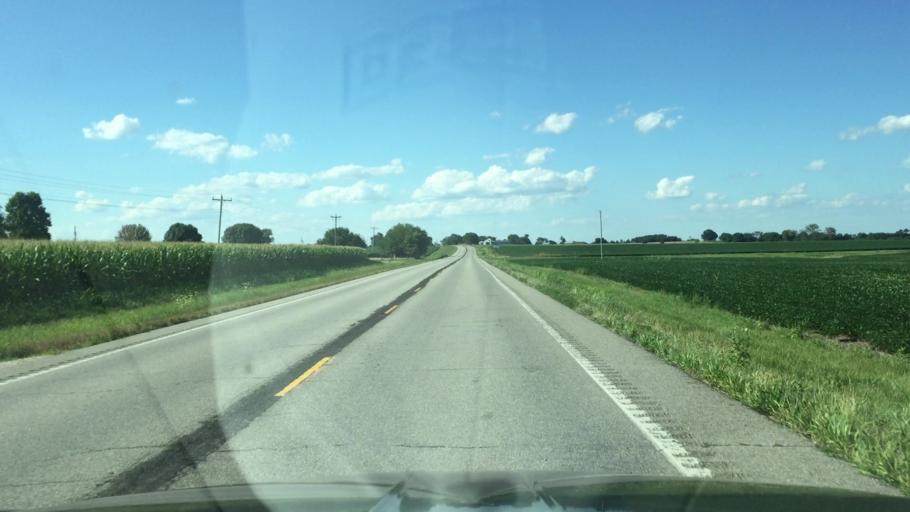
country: US
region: Missouri
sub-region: Moniteau County
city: Tipton
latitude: 38.5973
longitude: -92.7893
